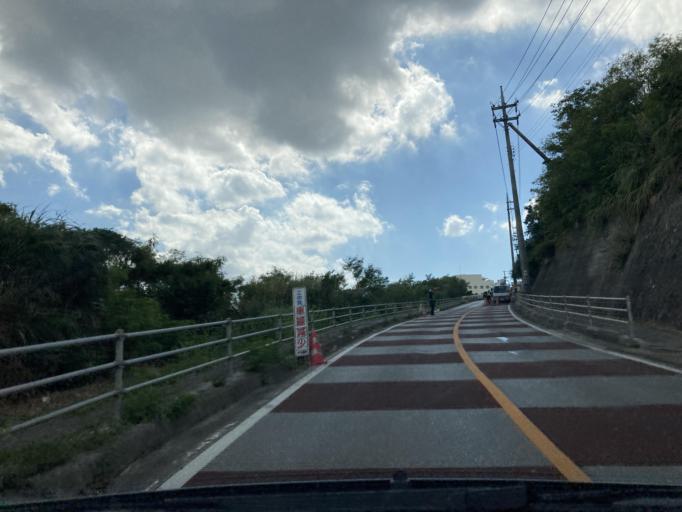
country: JP
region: Okinawa
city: Ginowan
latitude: 26.2504
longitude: 127.7765
